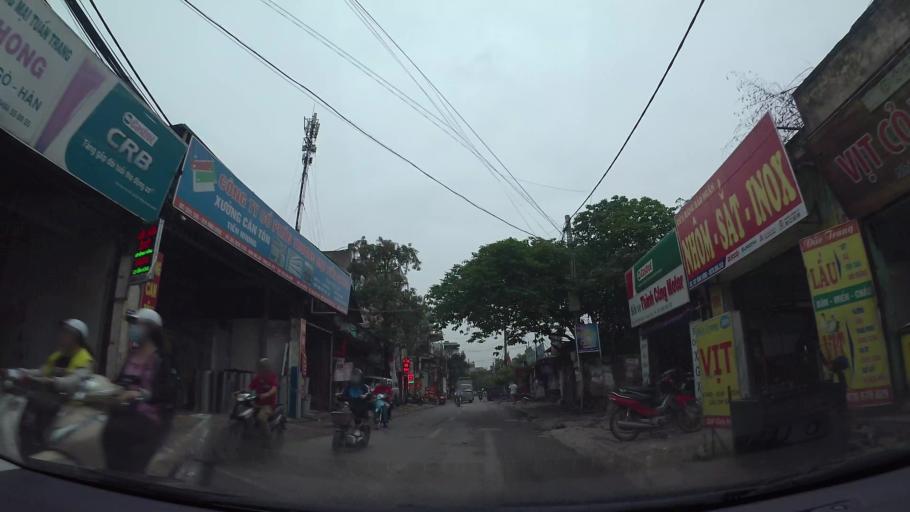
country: VN
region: Ha Noi
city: Hai BaTrung
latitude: 20.9937
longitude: 105.8798
